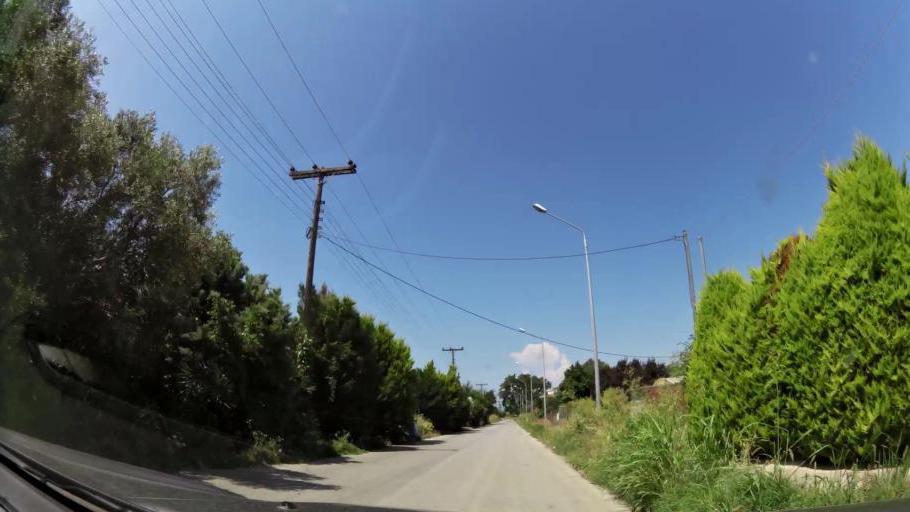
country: GR
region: Central Macedonia
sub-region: Nomos Thessalonikis
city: Nea Michaniona
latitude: 40.4950
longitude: 22.8269
